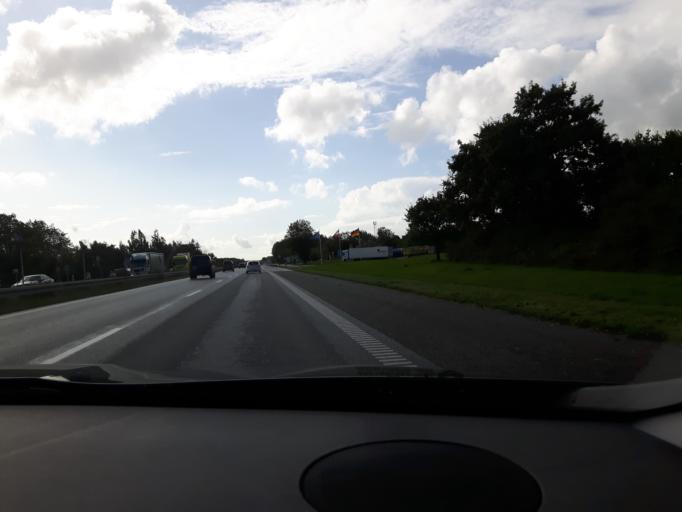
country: DE
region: Schleswig-Holstein
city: Handewitt
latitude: 54.8063
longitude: 9.3278
